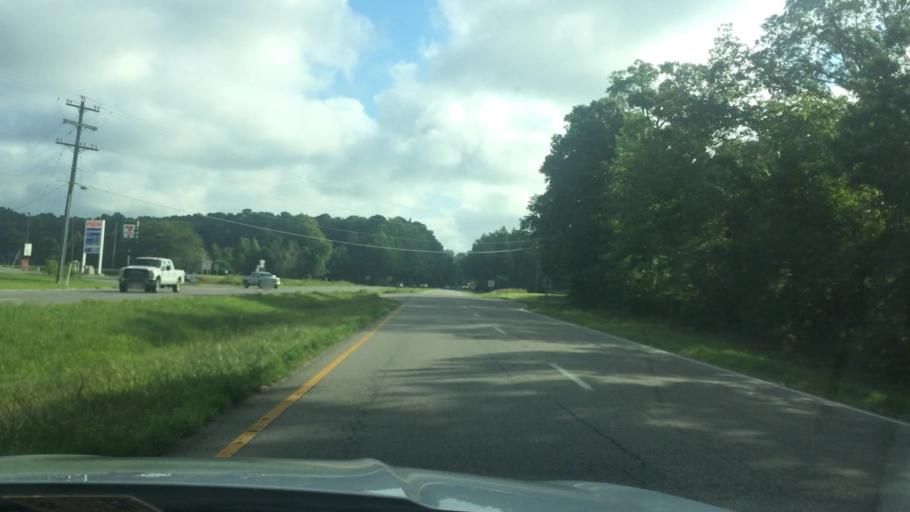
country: US
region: Virginia
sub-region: Gloucester County
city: Gloucester Courthouse
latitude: 37.4184
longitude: -76.5151
